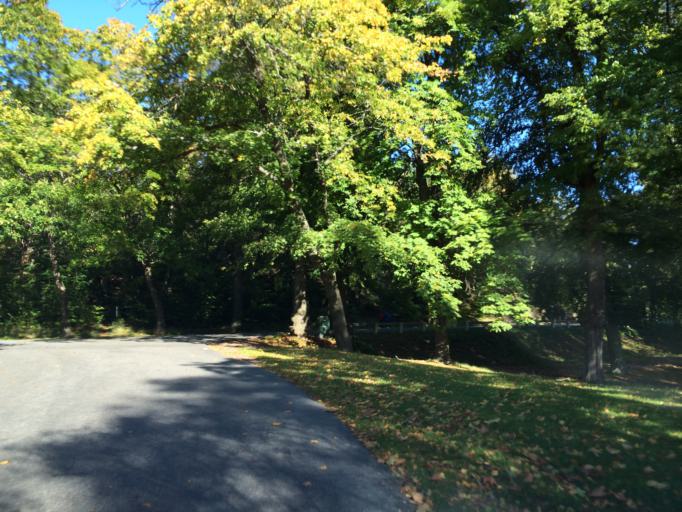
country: SE
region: Stockholm
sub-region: Nacka Kommun
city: Nacka
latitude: 59.3226
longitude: 18.1253
